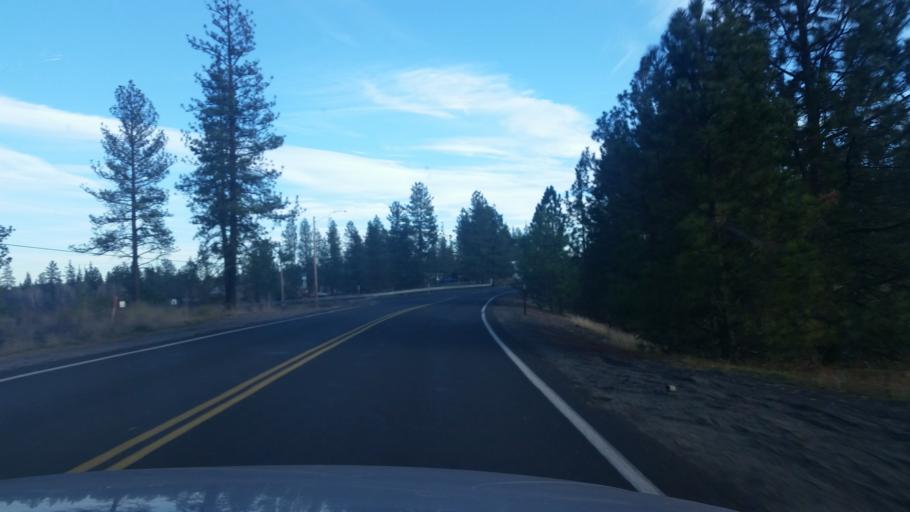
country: US
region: Washington
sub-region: Spokane County
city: Cheney
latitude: 47.4736
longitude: -117.5456
